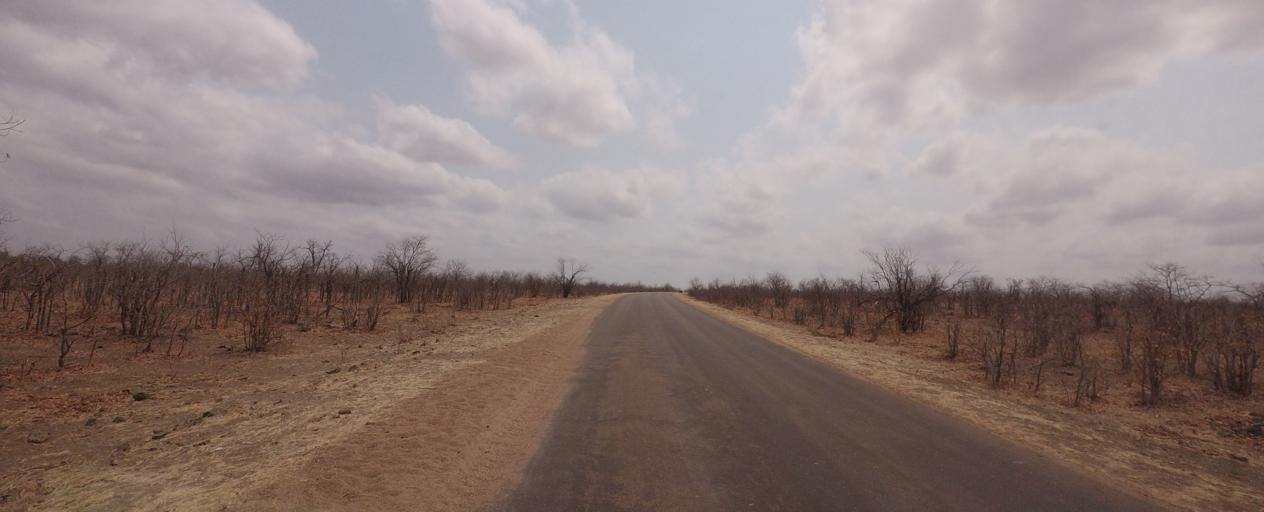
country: ZA
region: Limpopo
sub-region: Mopani District Municipality
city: Phalaborwa
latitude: -23.5851
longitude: 31.4504
